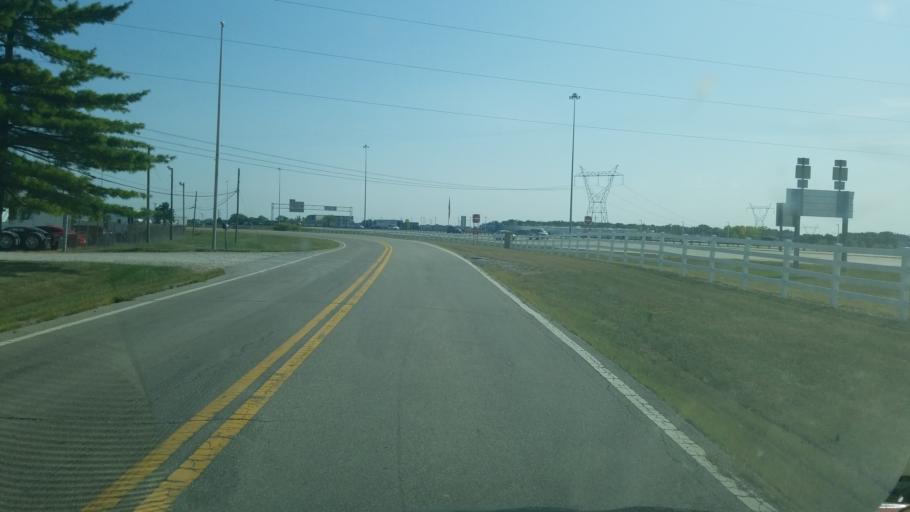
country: US
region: Ohio
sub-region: Franklin County
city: Grove City
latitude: 39.8425
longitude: -83.0901
